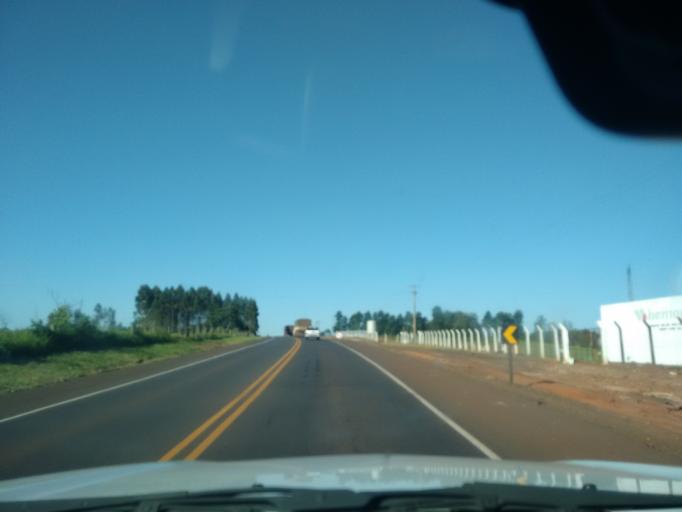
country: PY
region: Canindeyu
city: Salto del Guaira
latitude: -23.9628
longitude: -54.3221
